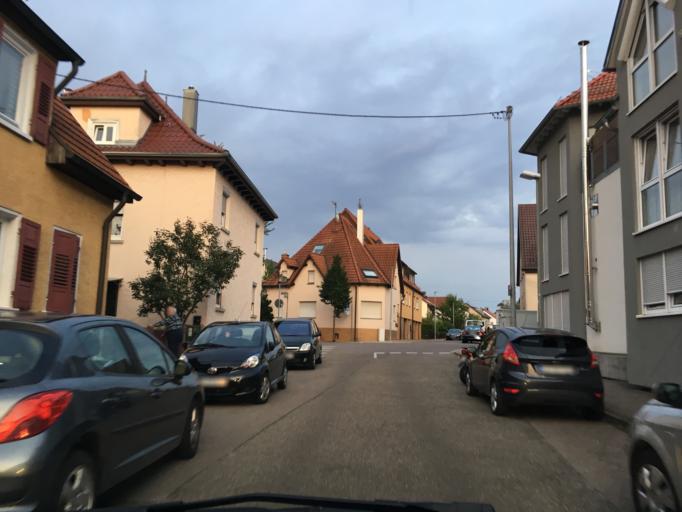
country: DE
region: Baden-Wuerttemberg
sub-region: Regierungsbezirk Stuttgart
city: Denkendorf
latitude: 48.7194
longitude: 9.3210
